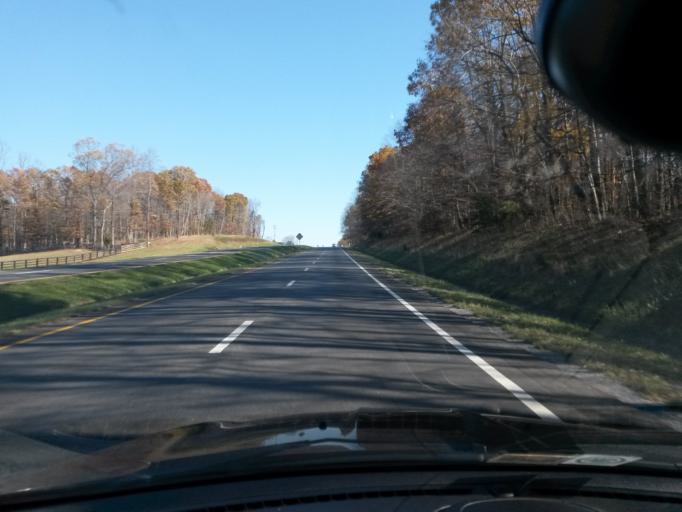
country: US
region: Virginia
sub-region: Campbell County
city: Timberlake
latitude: 37.3042
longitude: -79.3193
